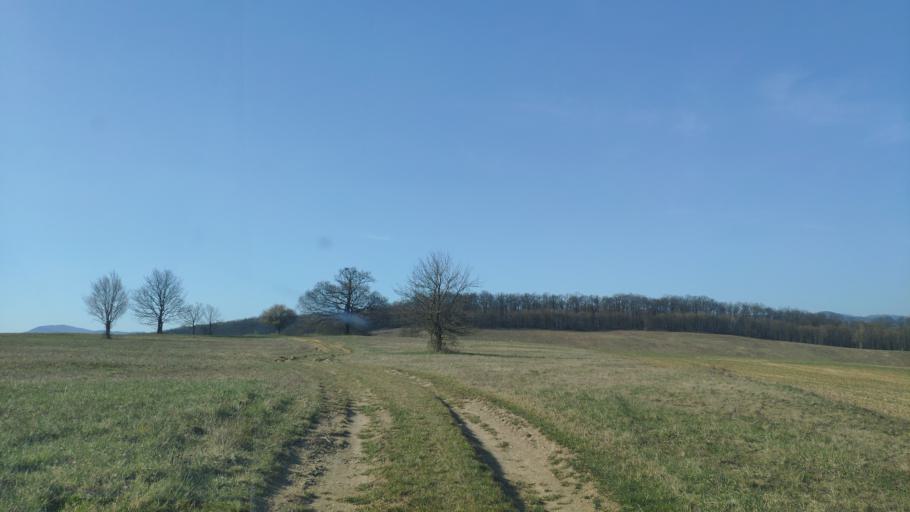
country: SK
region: Banskobystricky
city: Revuca
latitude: 48.5501
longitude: 20.2682
